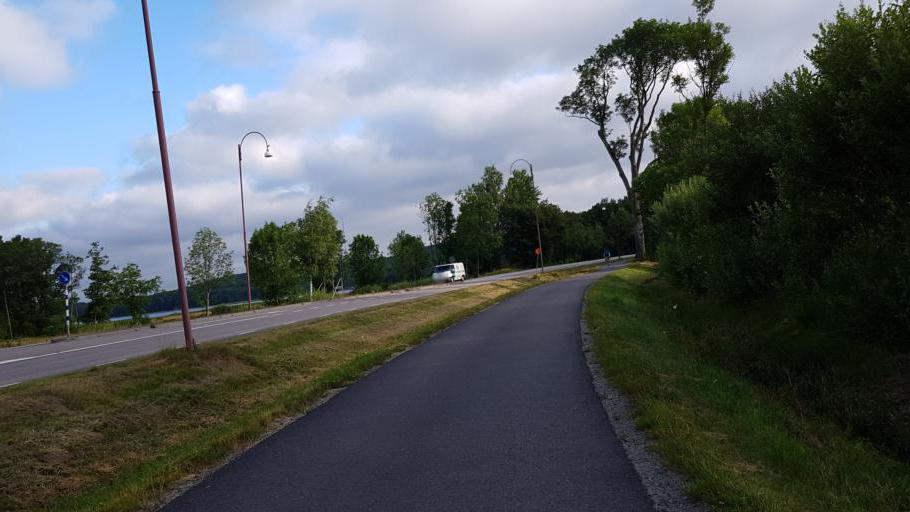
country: SE
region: Vaestra Goetaland
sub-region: Harryda Kommun
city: Molnlycke
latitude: 57.6621
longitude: 12.0924
